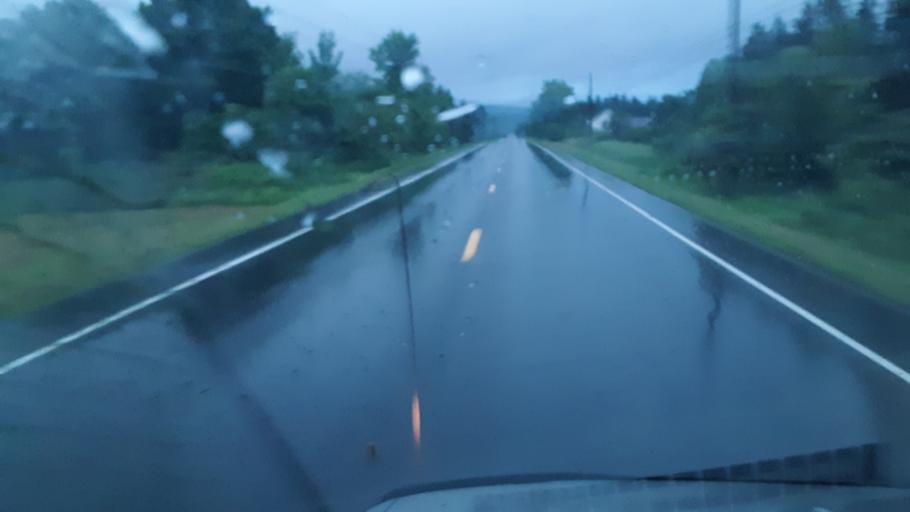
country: US
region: Maine
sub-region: Penobscot County
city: Patten
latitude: 45.9430
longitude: -68.4524
